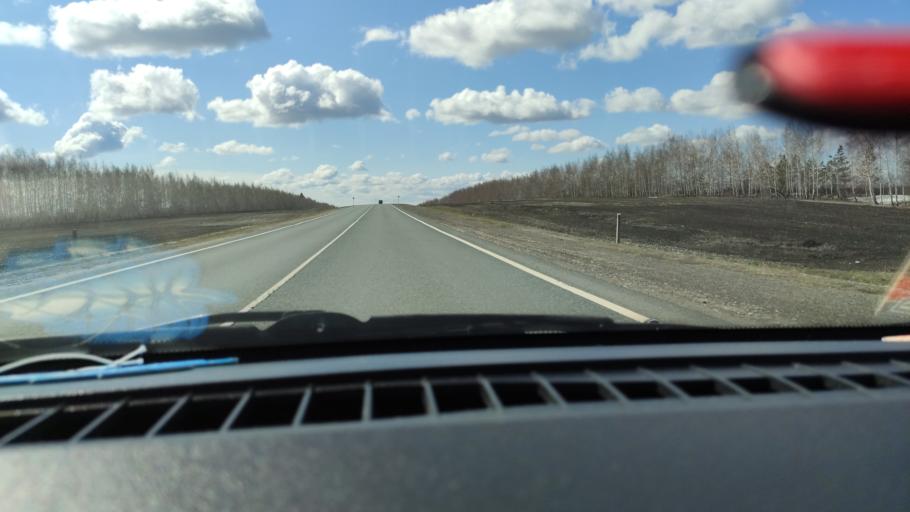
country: RU
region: Samara
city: Syzran'
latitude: 52.9079
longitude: 48.2987
